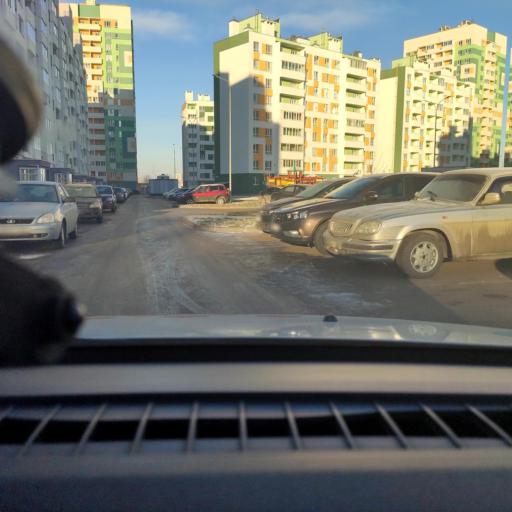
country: RU
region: Samara
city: Samara
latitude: 53.0958
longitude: 50.1642
